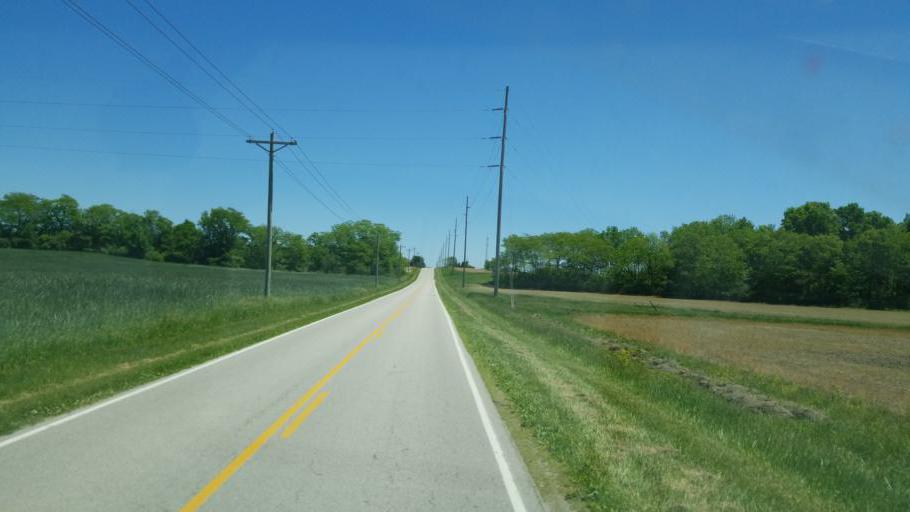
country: US
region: Ohio
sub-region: Darke County
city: Ansonia
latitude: 40.2648
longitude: -84.6478
